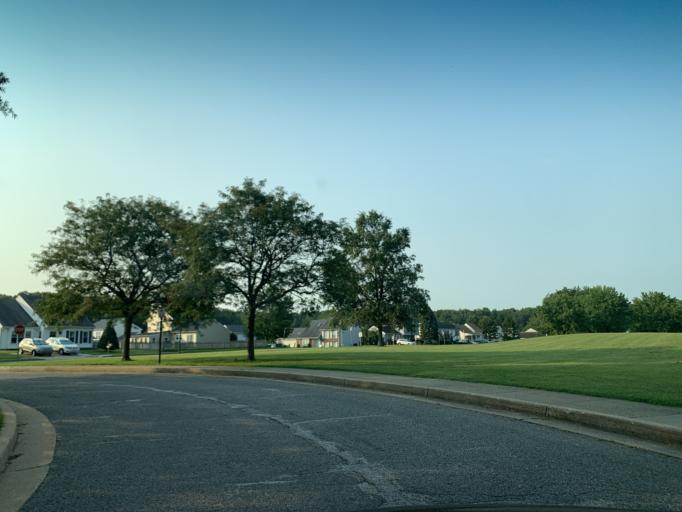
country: US
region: Maryland
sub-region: Baltimore County
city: Bowleys Quarters
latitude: 39.3694
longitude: -76.3540
